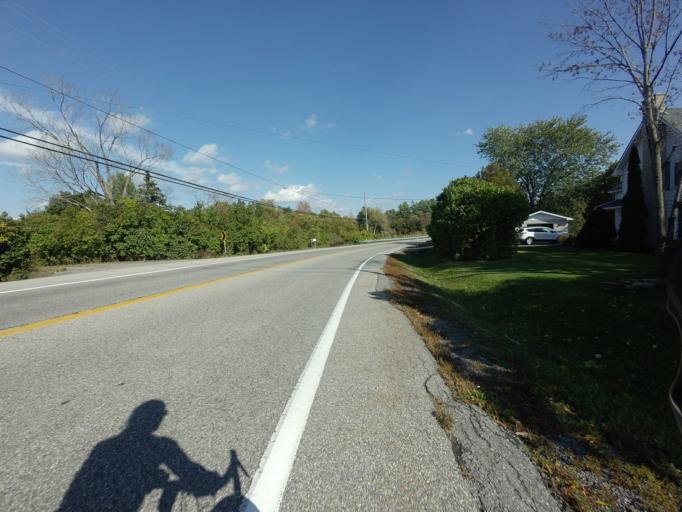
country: CA
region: Ontario
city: Kingston
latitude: 44.2166
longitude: -76.6890
